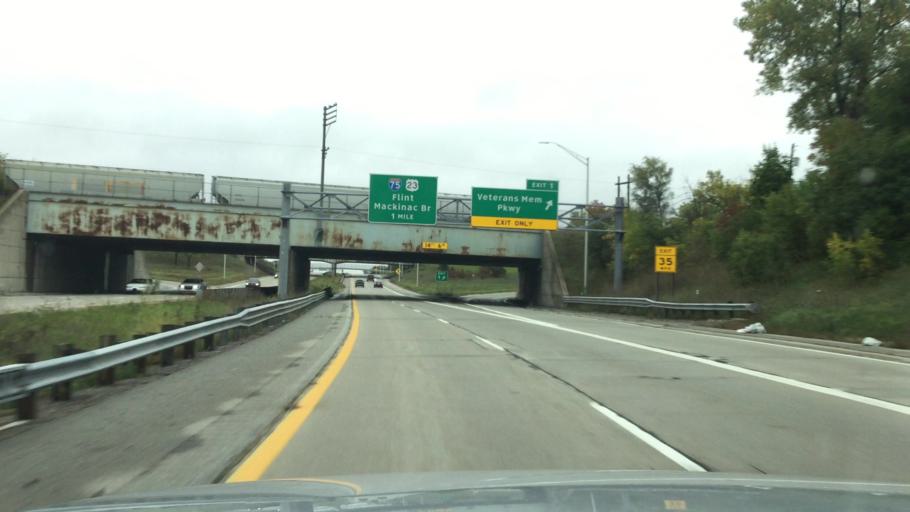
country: US
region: Michigan
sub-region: Saginaw County
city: Buena Vista
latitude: 43.4340
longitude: -83.9167
